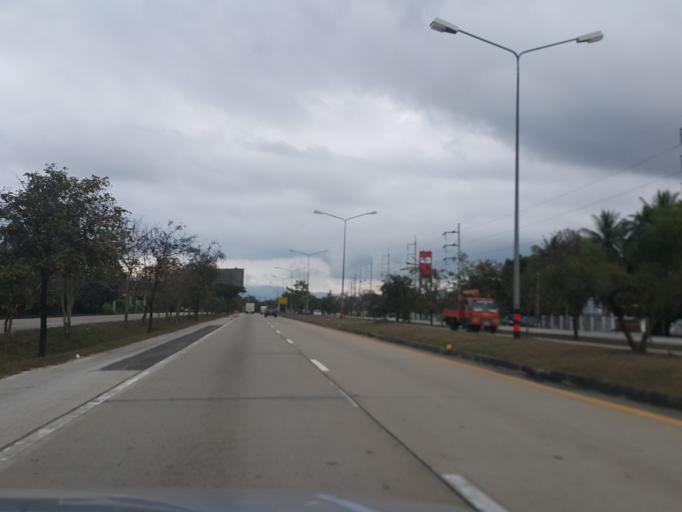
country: TH
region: Lampang
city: Lampang
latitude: 18.2892
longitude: 99.4393
